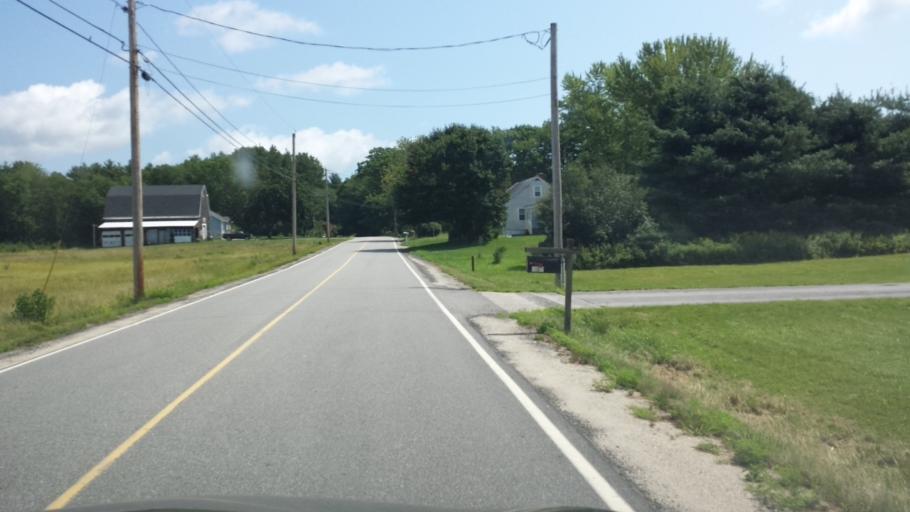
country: US
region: Maine
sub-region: York County
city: Kennebunk
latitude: 43.4456
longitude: -70.5239
